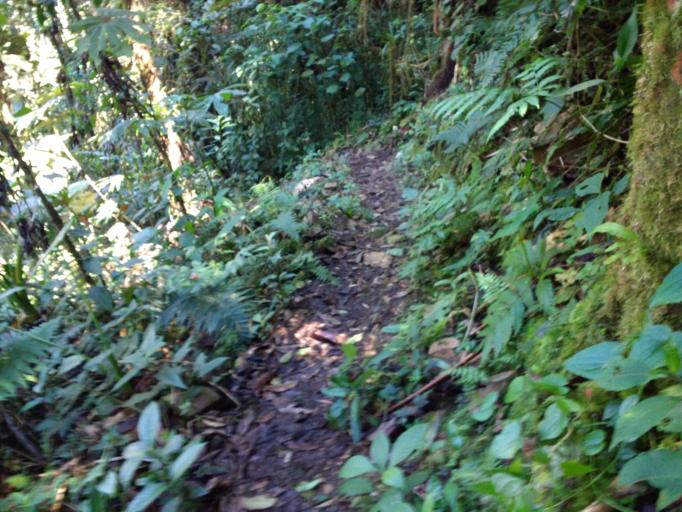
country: PE
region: Cusco
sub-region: Provincia de La Convencion
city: Maranura
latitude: -12.9724
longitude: -72.5306
